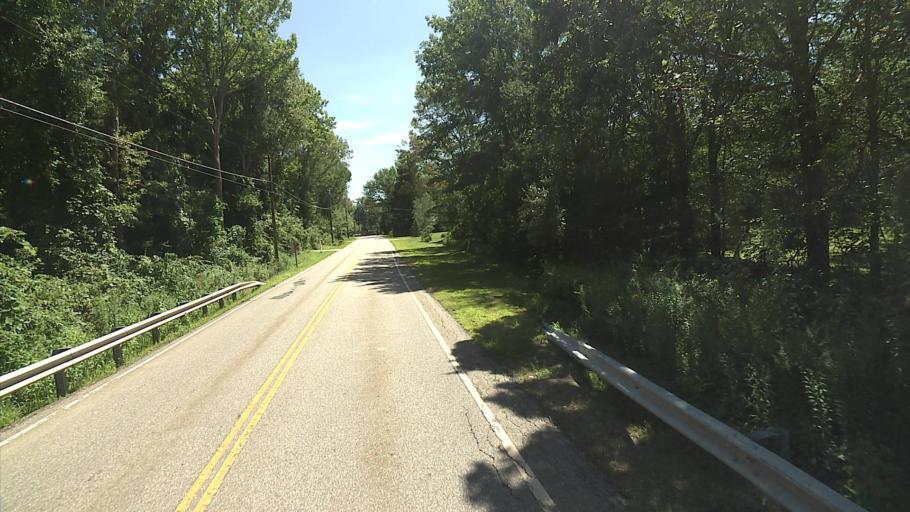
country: US
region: Connecticut
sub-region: Windham County
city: Windham
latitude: 41.7100
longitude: -72.0675
